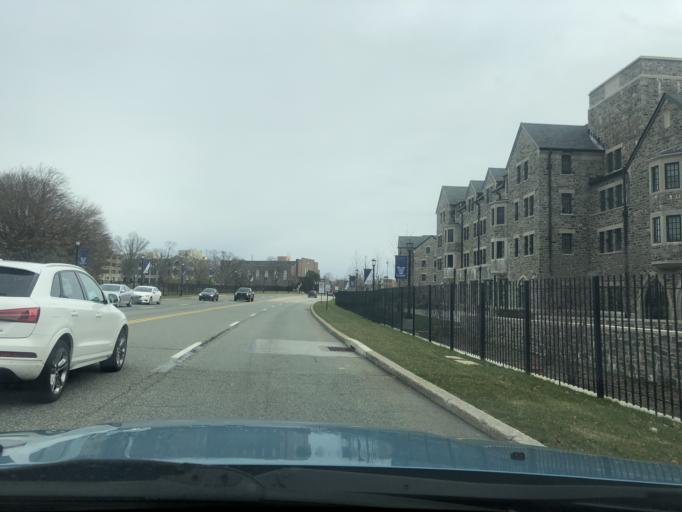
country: US
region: Pennsylvania
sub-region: Delaware County
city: Radnor
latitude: 40.0346
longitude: -75.3419
